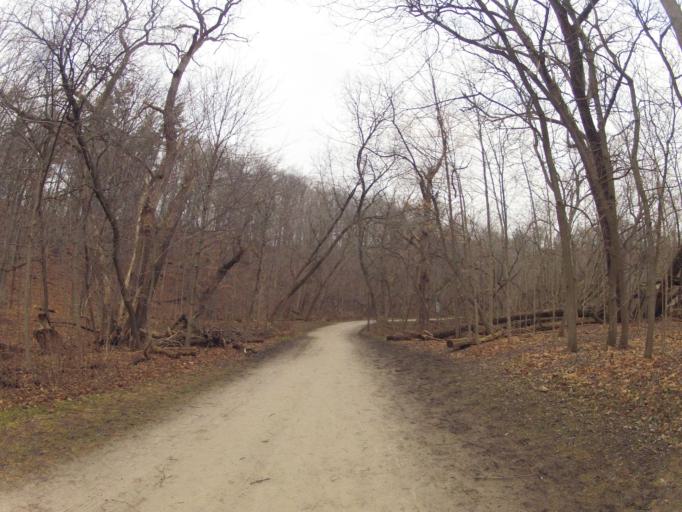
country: CA
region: Ontario
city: Mississauga
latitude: 43.5564
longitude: -79.6655
